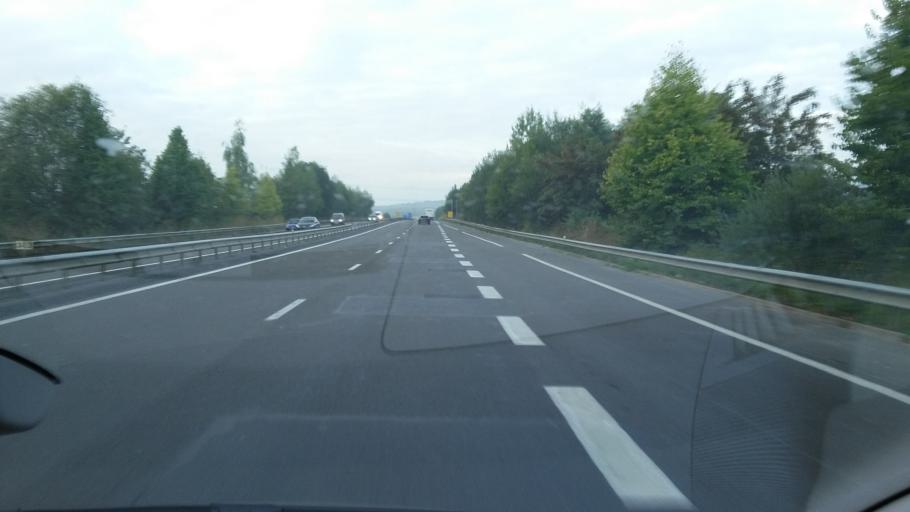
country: FR
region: Champagne-Ardenne
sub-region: Departement des Ardennes
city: La Francheville
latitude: 49.7257
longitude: 4.7119
